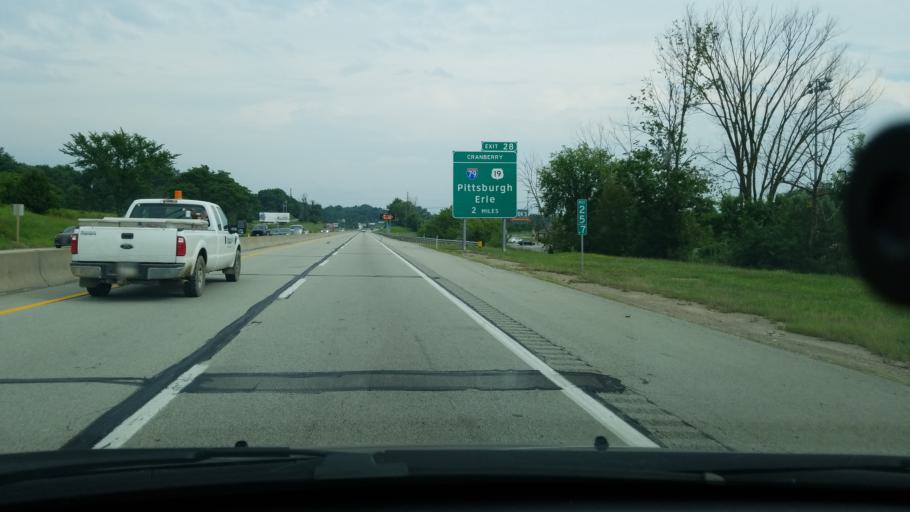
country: US
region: Pennsylvania
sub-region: Butler County
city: Fernway
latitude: 40.7131
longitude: -80.1317
